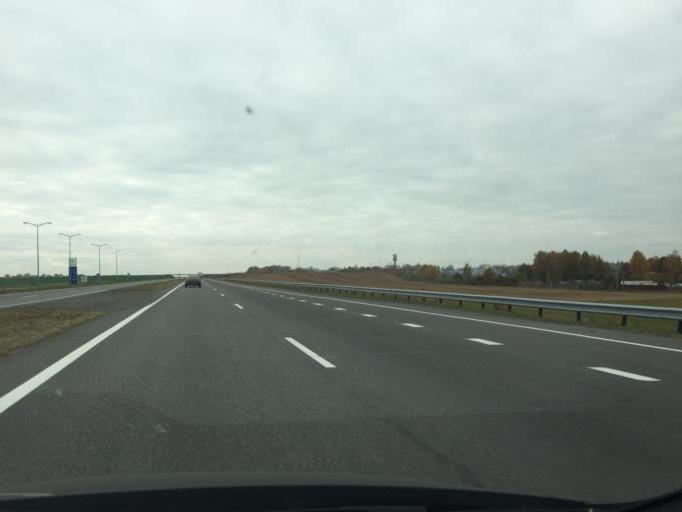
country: BY
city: Fanipol
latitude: 53.6942
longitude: 27.3814
